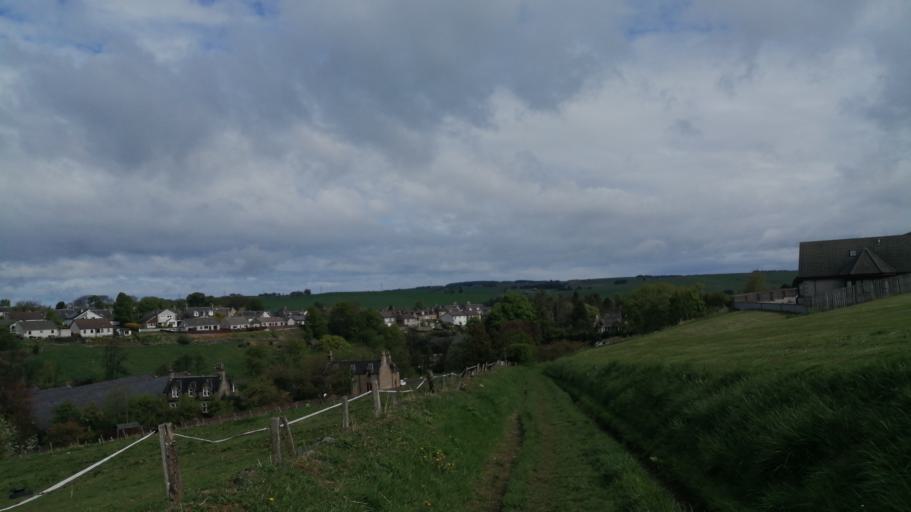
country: GB
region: Scotland
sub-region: Moray
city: Keith
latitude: 57.5395
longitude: -2.9592
